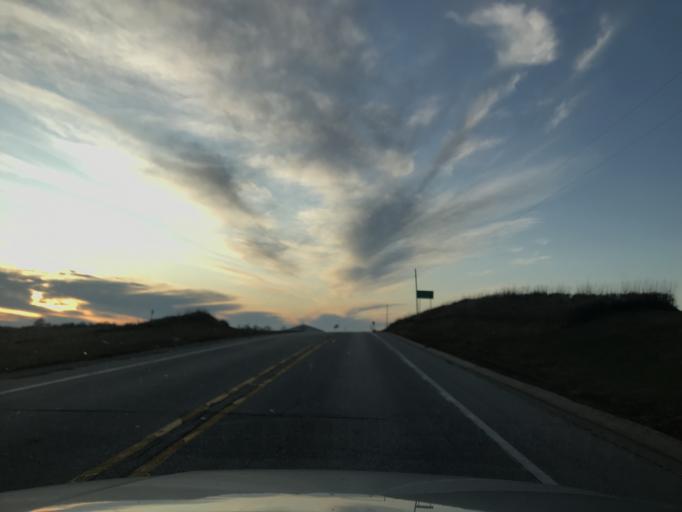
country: US
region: Illinois
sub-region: Henderson County
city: Oquawka
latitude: 41.0186
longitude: -90.8506
